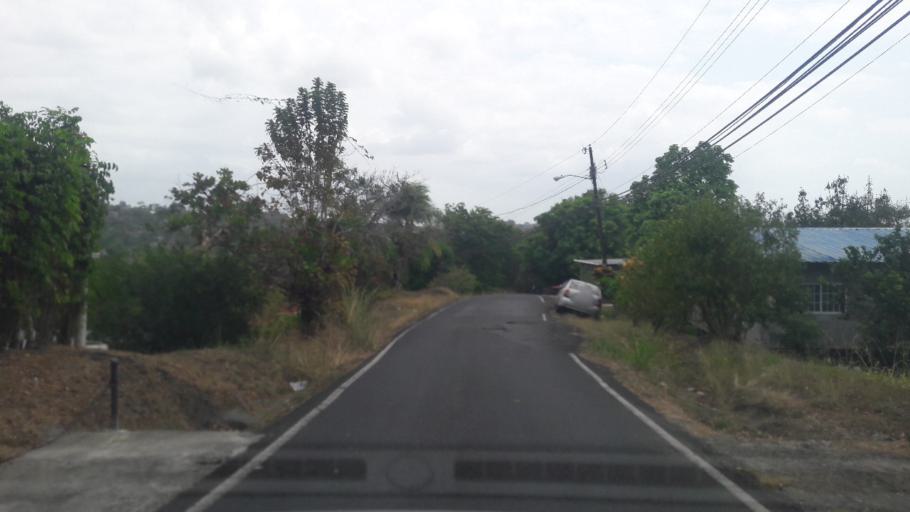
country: PA
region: Panama
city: Alcalde Diaz
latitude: 9.1241
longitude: -79.5491
